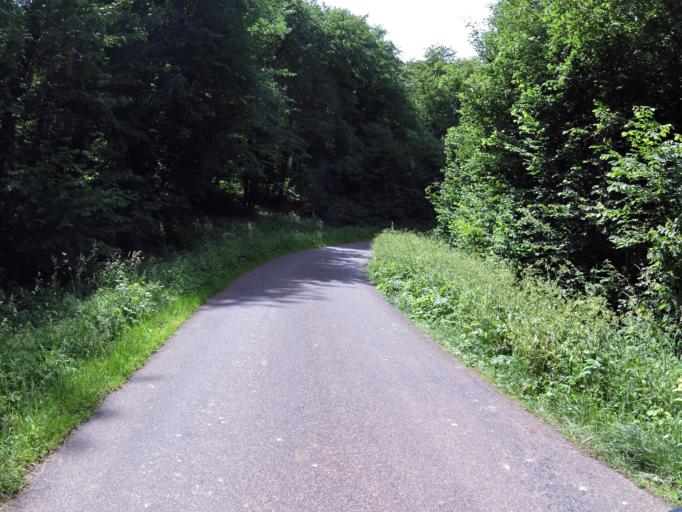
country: FR
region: Lorraine
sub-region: Departement de la Meuse
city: Stenay
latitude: 49.5389
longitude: 5.1377
